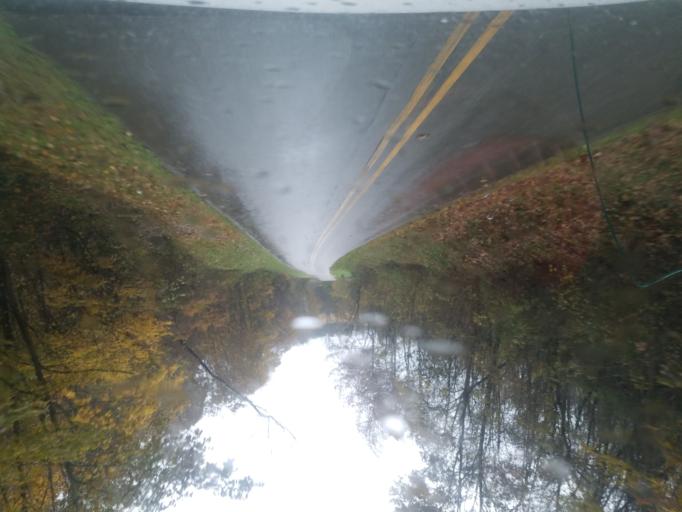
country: US
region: Ohio
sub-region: Washington County
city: Beverly
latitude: 39.4631
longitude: -81.6286
